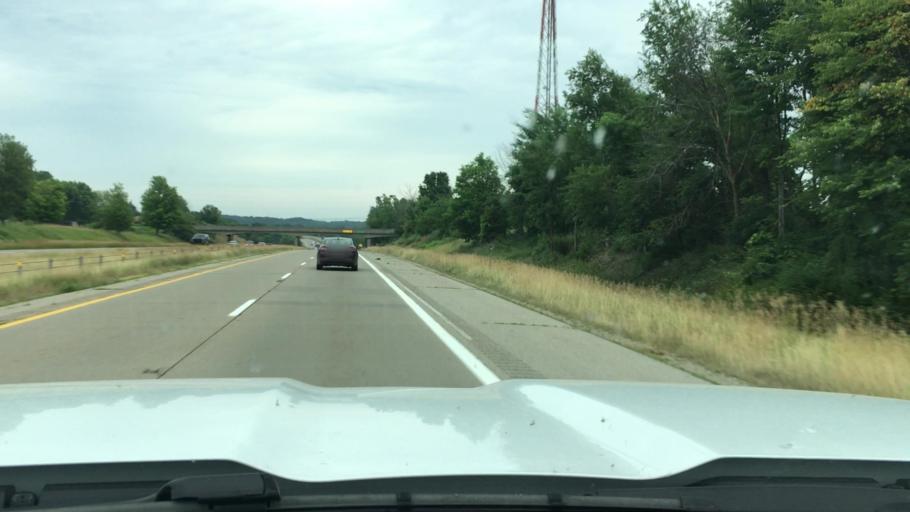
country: US
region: Michigan
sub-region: Ionia County
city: Portland
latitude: 42.8624
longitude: -84.9254
